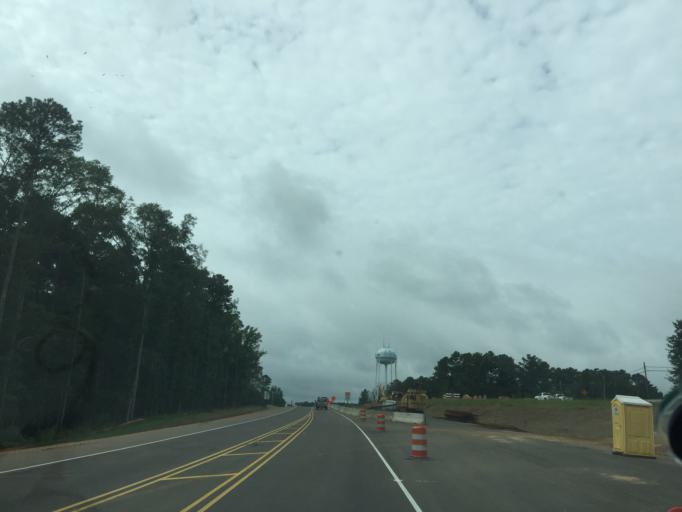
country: US
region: Mississippi
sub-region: Rankin County
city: Brandon
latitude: 32.2818
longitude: -89.9932
